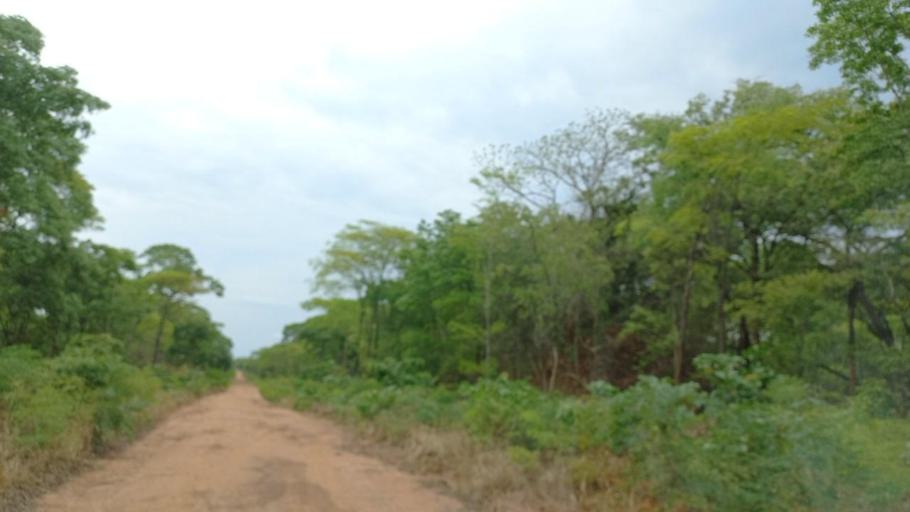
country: ZM
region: North-Western
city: Kalengwa
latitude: -13.5841
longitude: 24.9717
